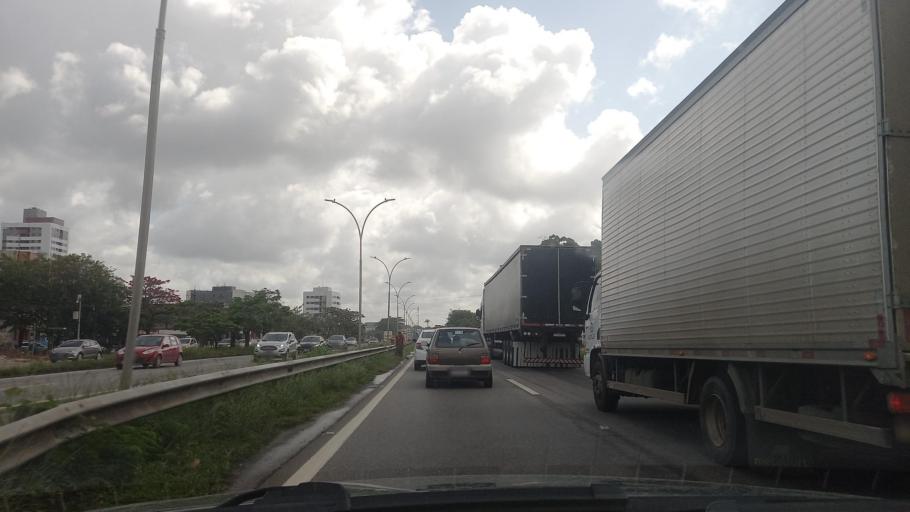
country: BR
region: Pernambuco
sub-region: Recife
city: Recife
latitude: -8.0443
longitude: -34.9433
